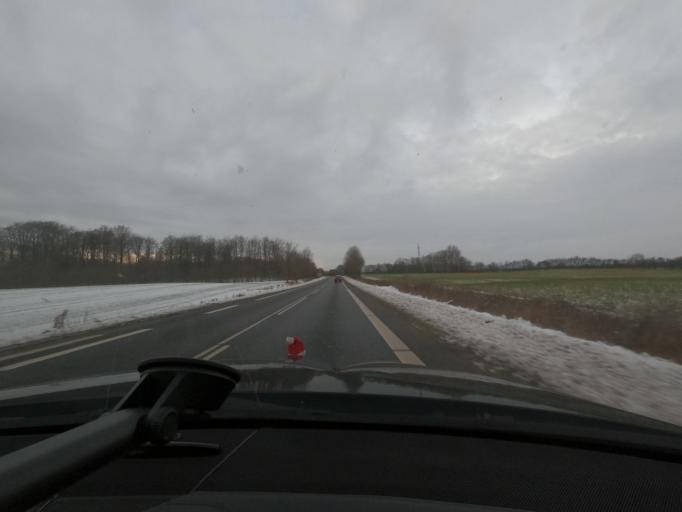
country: DE
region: Schleswig-Holstein
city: Wees
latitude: 54.8871
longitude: 9.4934
